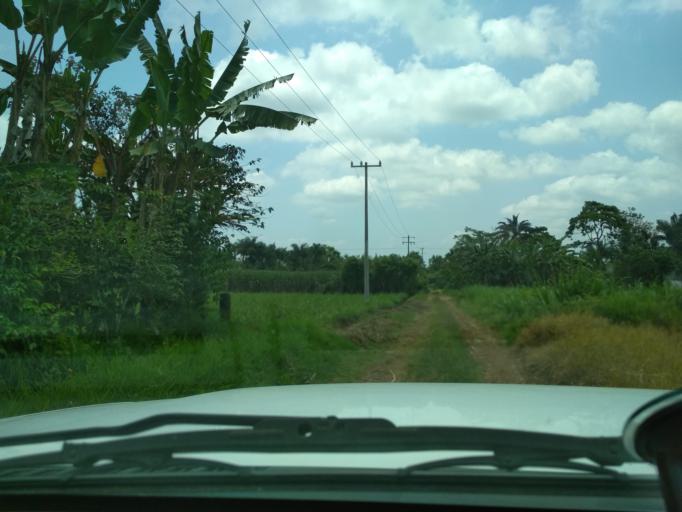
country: MX
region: Veracruz
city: Tocuila
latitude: 18.9567
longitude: -97.0152
